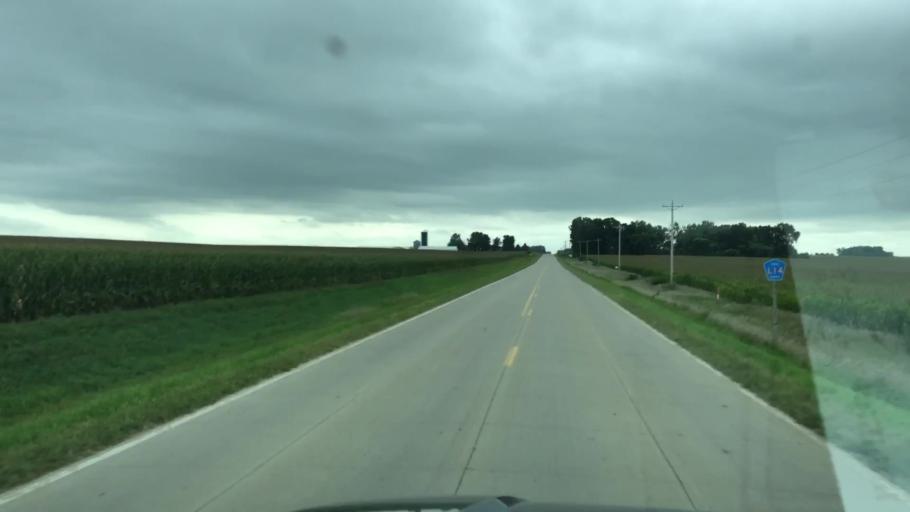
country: US
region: Iowa
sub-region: Sioux County
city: Alton
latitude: 43.0983
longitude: -95.9784
